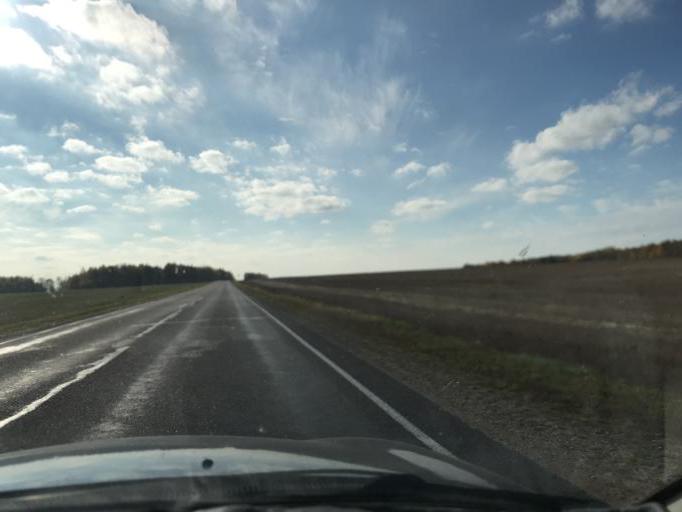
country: BY
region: Grodnenskaya
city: Voranava
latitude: 54.1956
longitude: 25.3458
